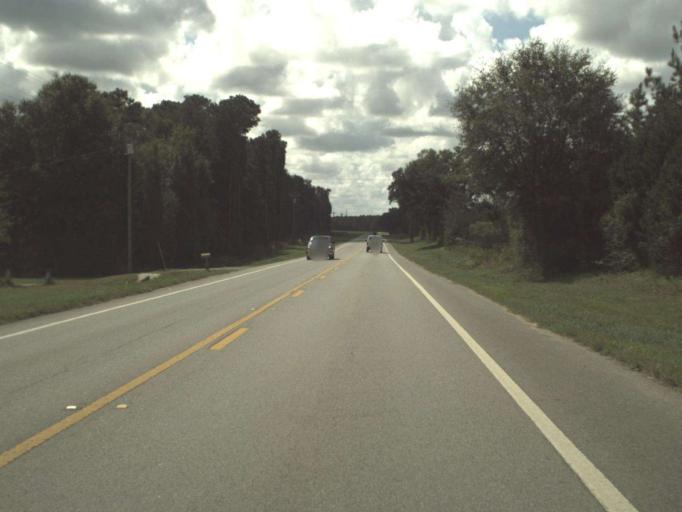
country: US
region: Florida
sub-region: Jackson County
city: Graceville
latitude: 30.9212
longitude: -85.4285
